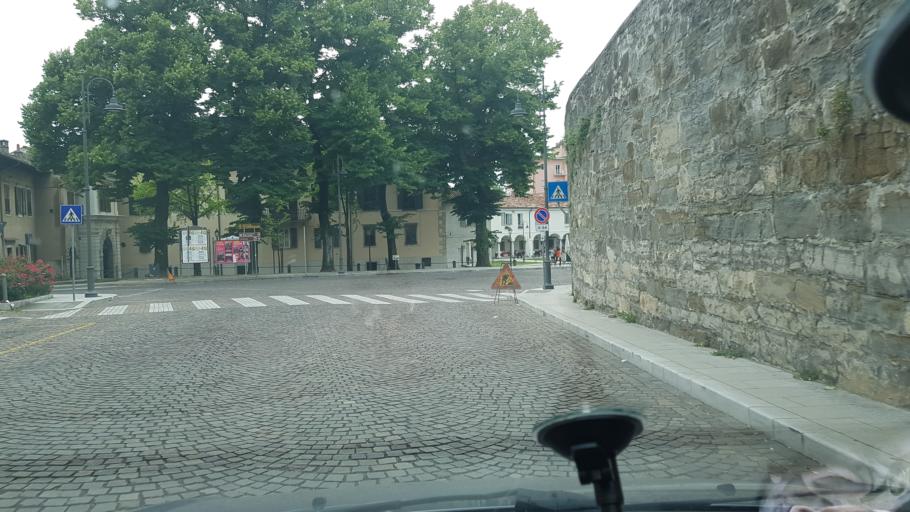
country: IT
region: Friuli Venezia Giulia
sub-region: Provincia di Gorizia
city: Gorizia
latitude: 45.9415
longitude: 13.6273
